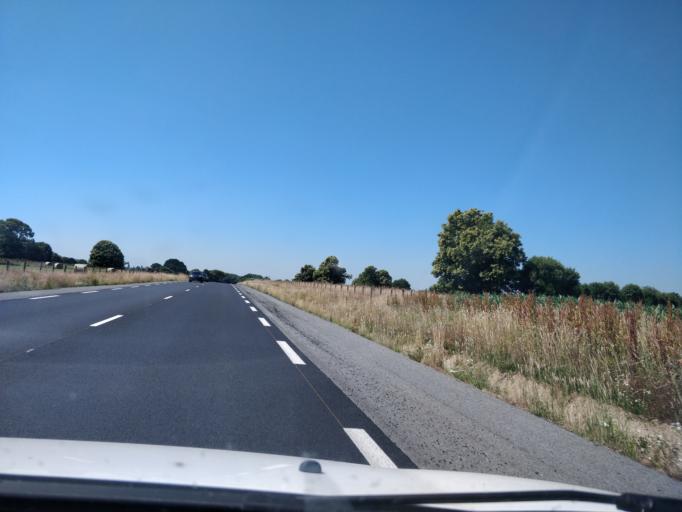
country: FR
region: Brittany
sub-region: Departement d'Ille-et-Vilaine
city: Dol-de-Bretagne
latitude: 48.5279
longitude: -1.7407
